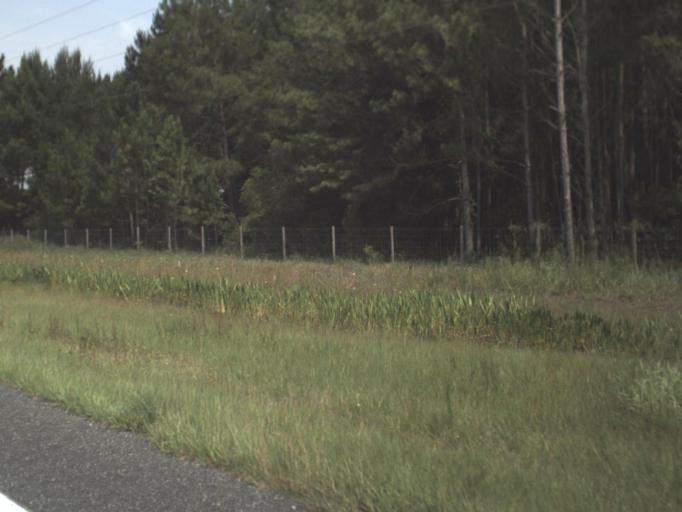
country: US
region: Florida
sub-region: Levy County
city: Bronson
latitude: 29.4761
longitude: -82.7237
